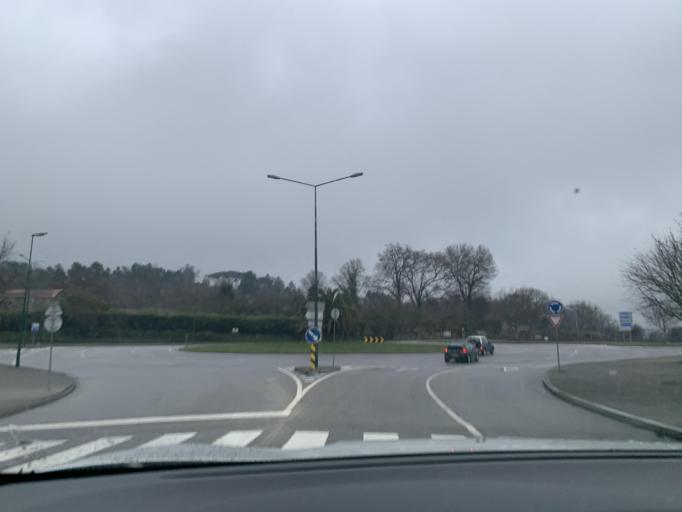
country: PT
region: Viseu
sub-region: Viseu
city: Viseu
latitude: 40.6490
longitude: -7.9020
